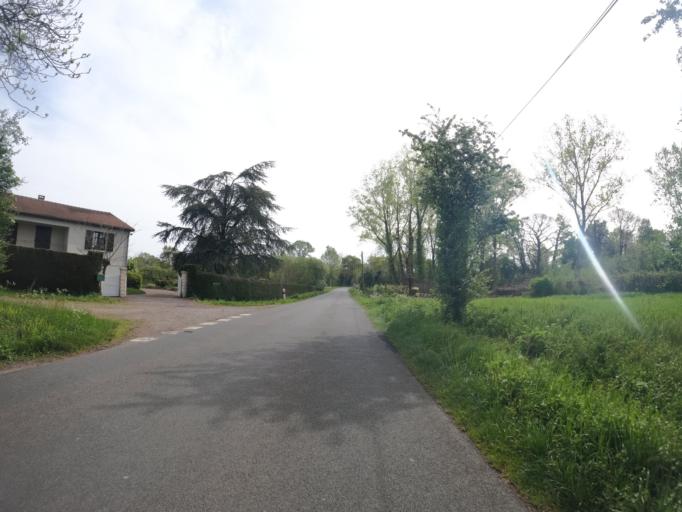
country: FR
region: Poitou-Charentes
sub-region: Departement des Deux-Sevres
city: La Chapelle-Saint-Laurent
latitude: 46.6953
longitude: -0.5070
